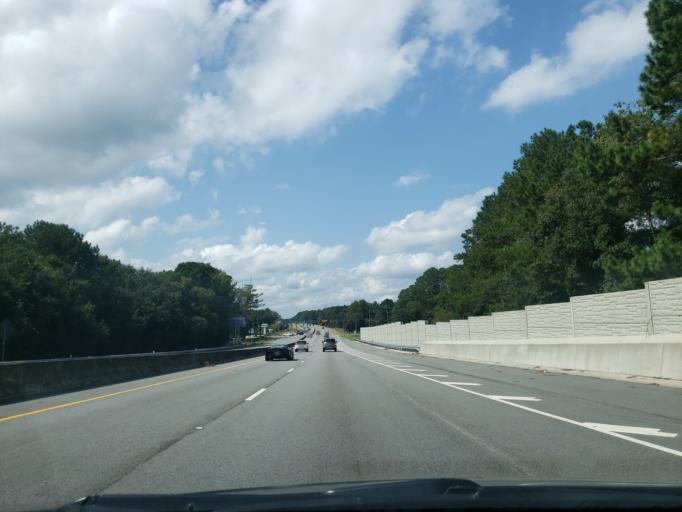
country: US
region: Georgia
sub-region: Chatham County
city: Georgetown
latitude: 31.9906
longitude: -81.2248
